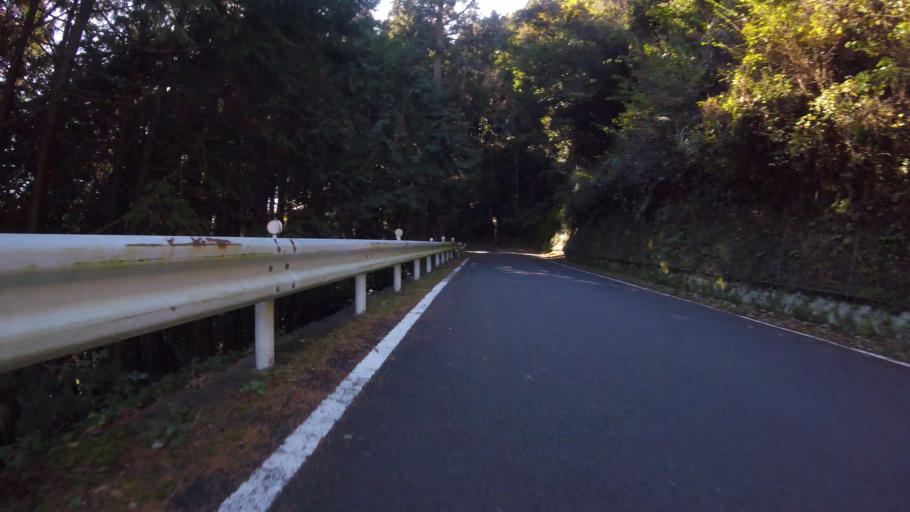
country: JP
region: Shizuoka
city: Shimoda
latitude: 34.7666
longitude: 138.9721
